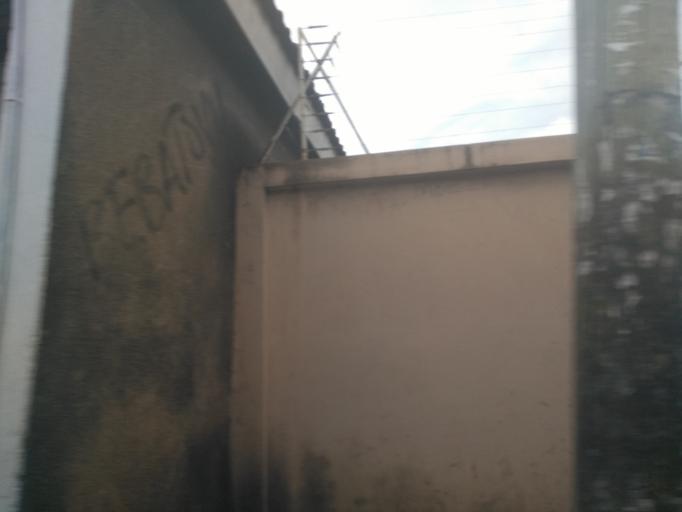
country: TZ
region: Dar es Salaam
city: Magomeni
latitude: -6.7961
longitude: 39.2675
